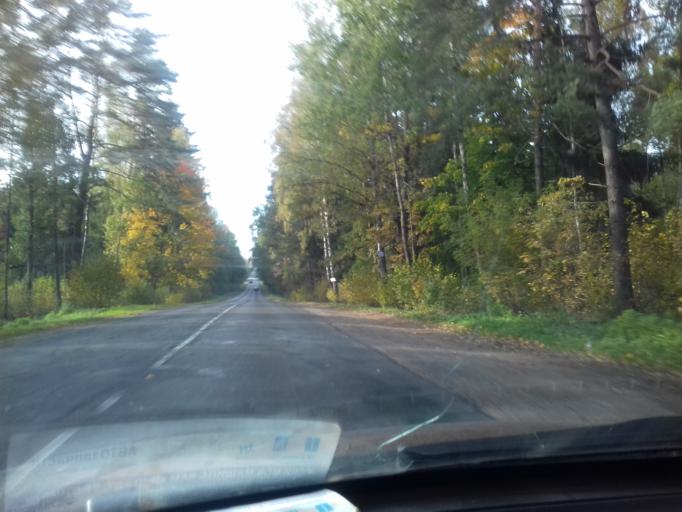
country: BY
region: Minsk
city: Hatava
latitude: 53.7591
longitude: 27.6526
